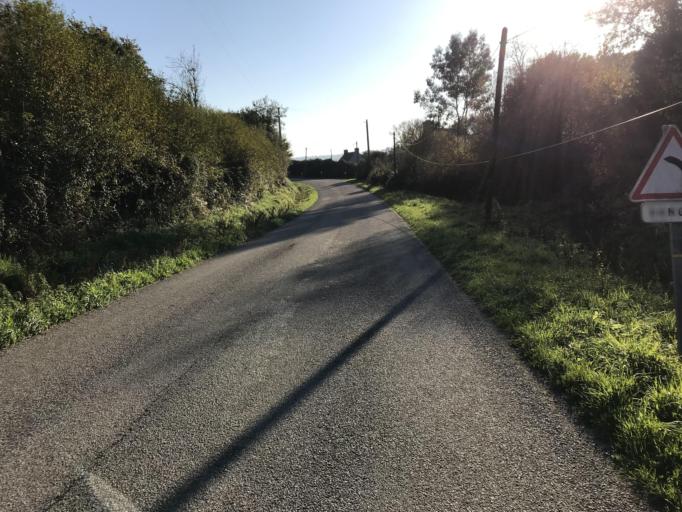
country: FR
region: Brittany
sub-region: Departement du Finistere
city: Hopital-Camfrout
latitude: 48.3028
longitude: -4.2339
